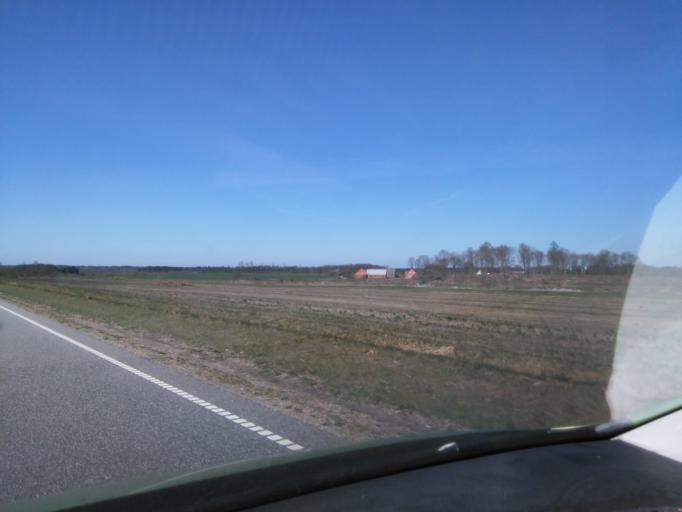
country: DK
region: South Denmark
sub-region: Vejle Kommune
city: Give
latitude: 55.8108
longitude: 9.2304
